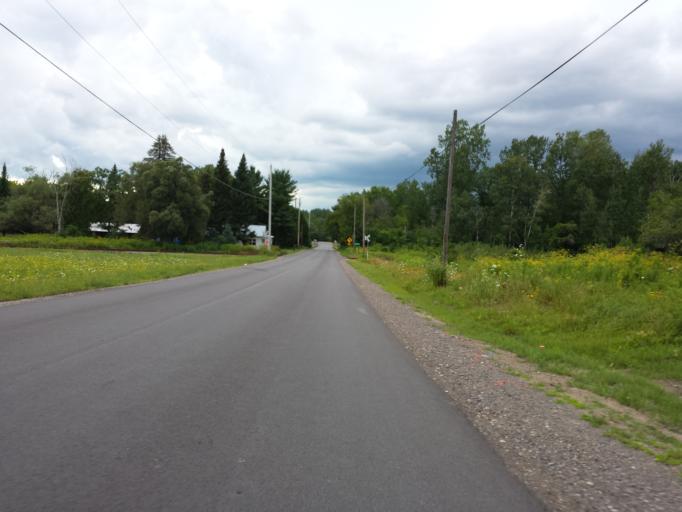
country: US
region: New York
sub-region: St. Lawrence County
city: Potsdam
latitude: 44.7055
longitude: -75.0019
